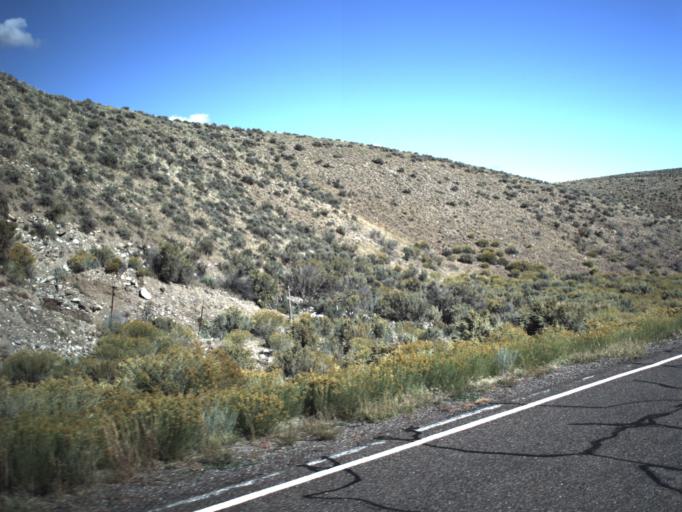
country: US
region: Utah
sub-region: Piute County
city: Junction
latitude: 38.3545
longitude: -111.9461
